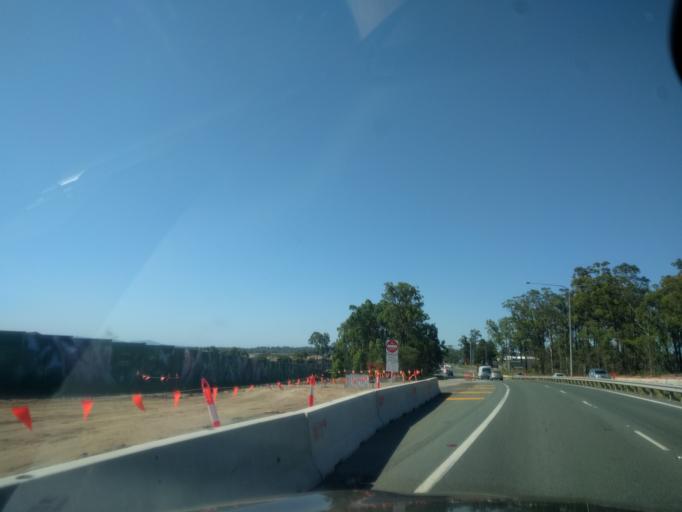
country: AU
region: Queensland
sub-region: Brisbane
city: Sunnybank Hills
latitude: -27.6407
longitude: 153.0443
